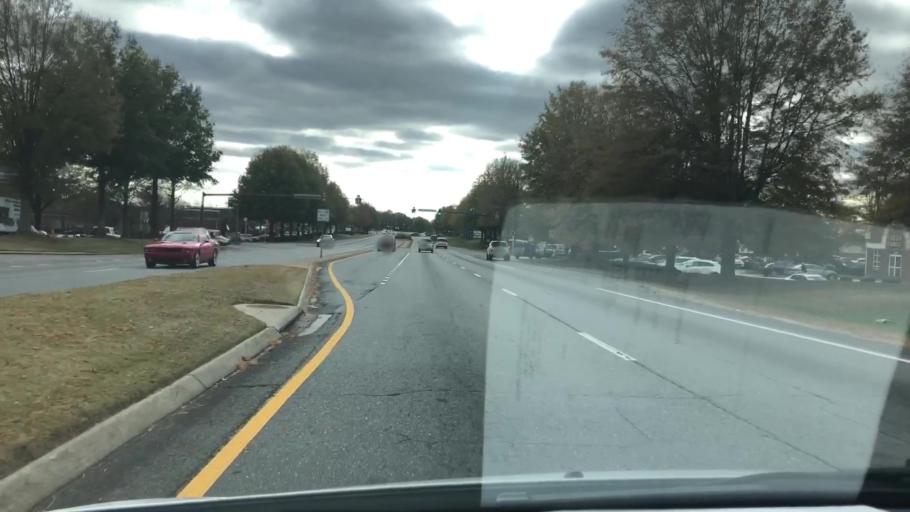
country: US
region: Georgia
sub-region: Fulton County
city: Johns Creek
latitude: 34.0731
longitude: -84.1661
